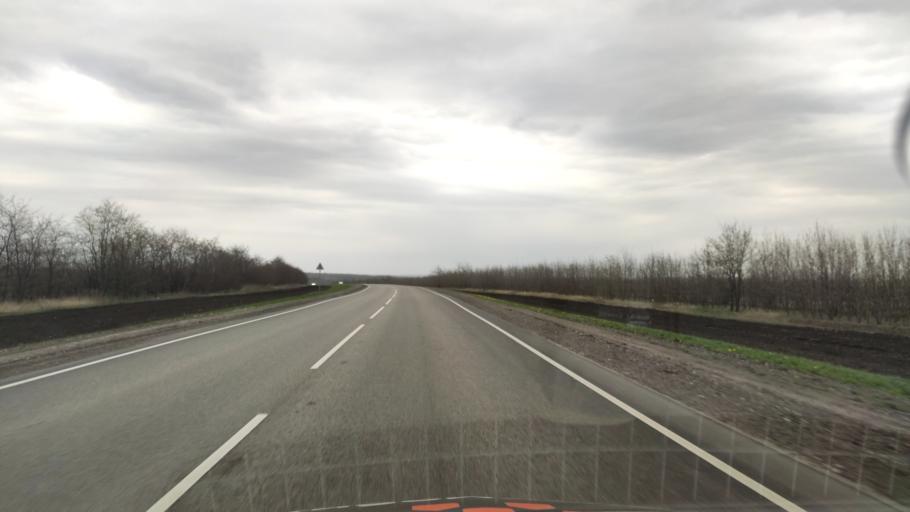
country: RU
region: Voronezj
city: Nizhnedevitsk
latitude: 51.5681
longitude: 38.3398
